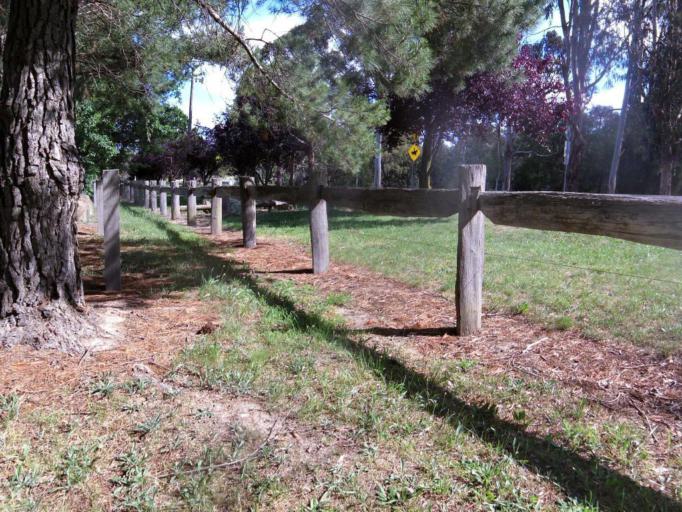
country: AU
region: Australian Capital Territory
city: Belconnen
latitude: -35.1713
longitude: 149.0708
